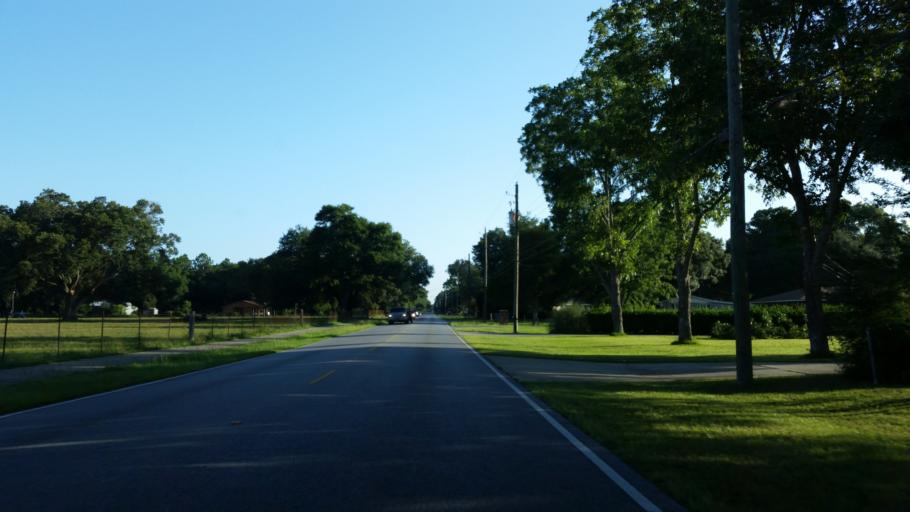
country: US
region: Florida
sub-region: Escambia County
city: Bellview
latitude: 30.4764
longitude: -87.2983
